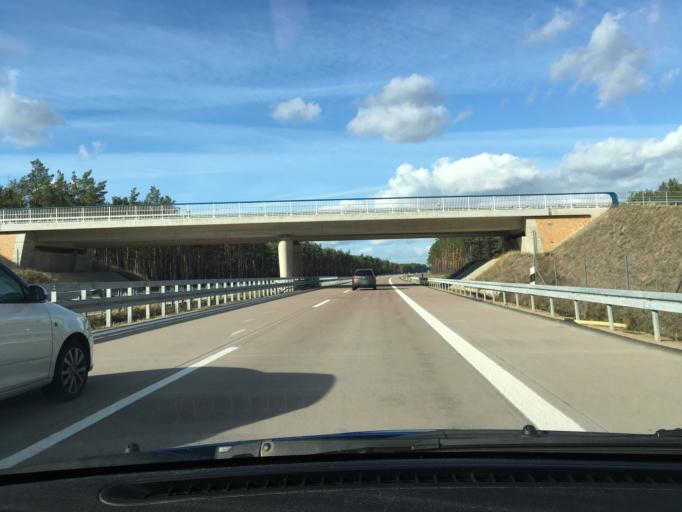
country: DE
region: Mecklenburg-Vorpommern
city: Grabow
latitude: 53.2772
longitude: 11.5274
